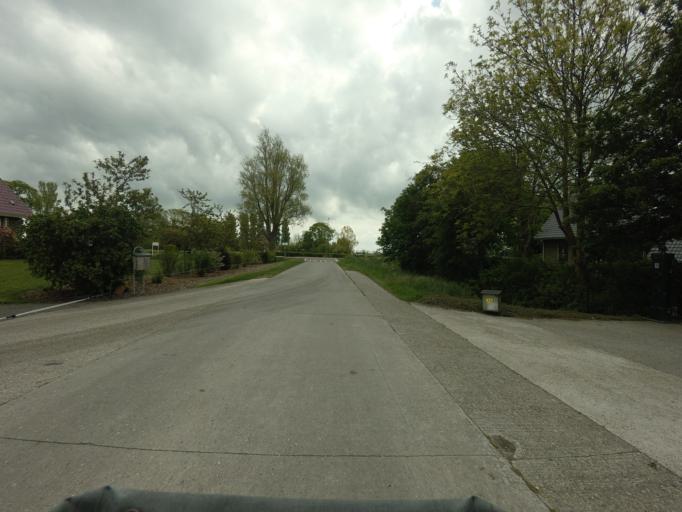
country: NL
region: Friesland
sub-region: Gemeente Littenseradiel
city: Wommels
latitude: 53.1030
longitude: 5.6238
